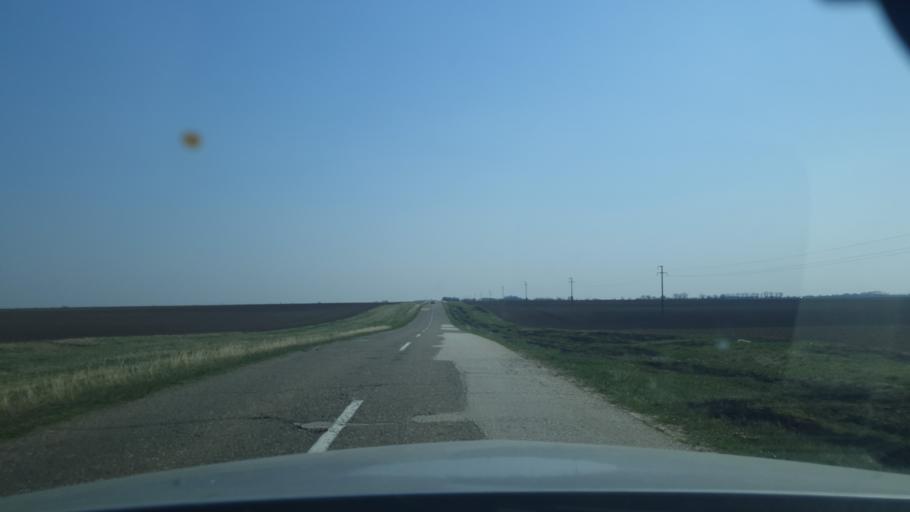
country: RS
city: Sasinci
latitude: 45.0313
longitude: 19.7498
